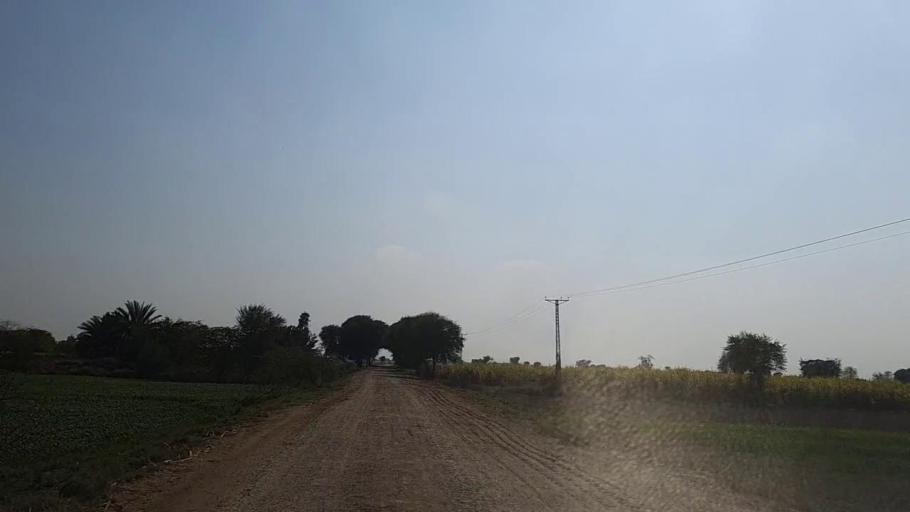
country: PK
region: Sindh
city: Daur
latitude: 26.4501
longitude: 68.2347
